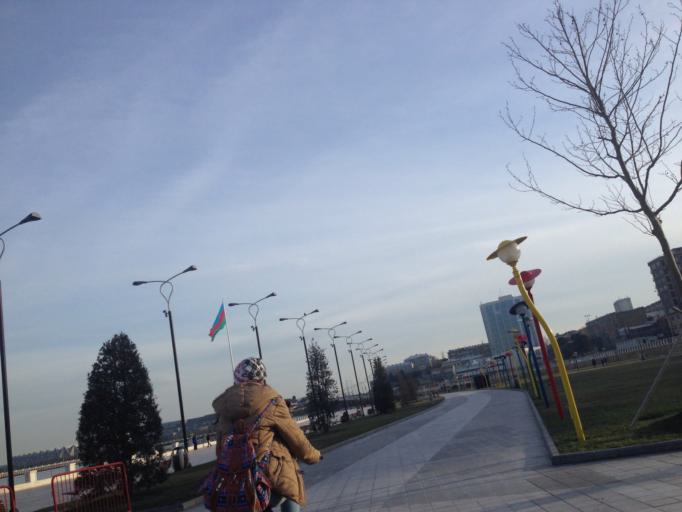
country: AZ
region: Baki
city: Badamdar
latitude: 40.3504
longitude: 49.8369
